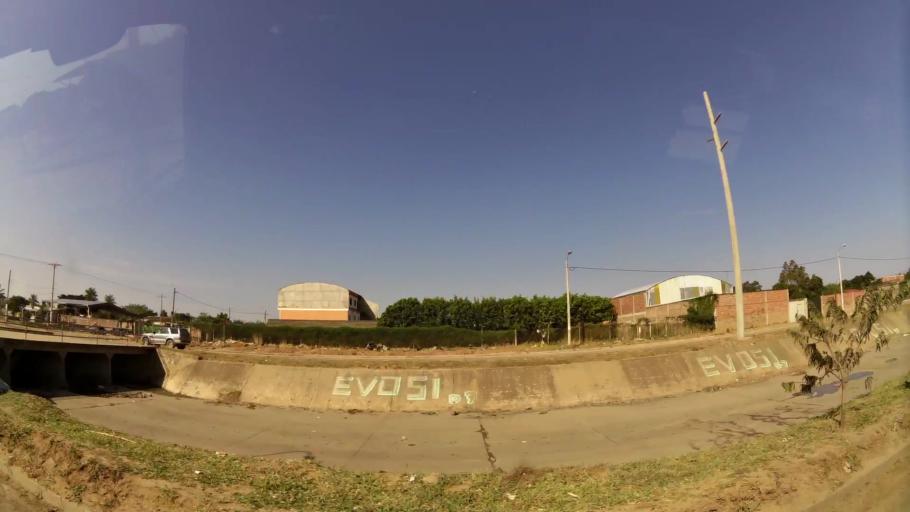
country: BO
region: Santa Cruz
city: Cotoca
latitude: -17.7984
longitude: -63.1090
